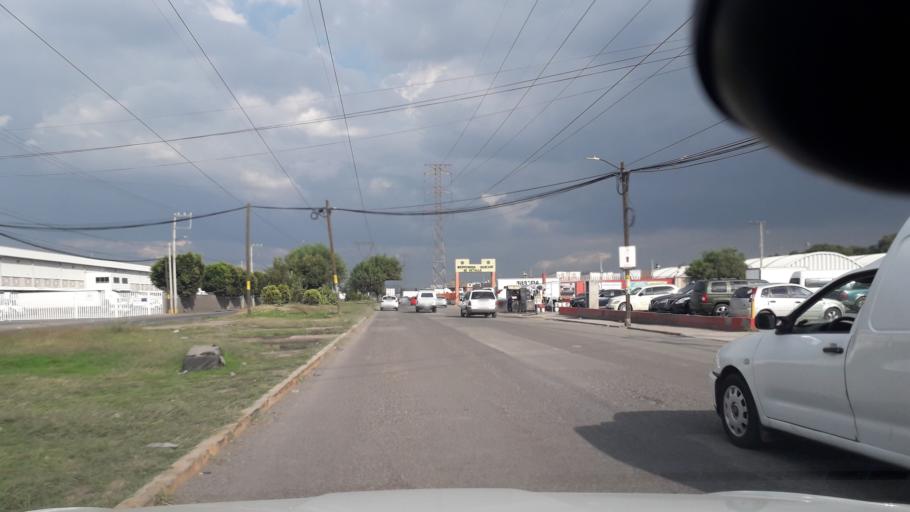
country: MX
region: Mexico
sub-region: Tultitlan
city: Fuentes del Valle
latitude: 19.6398
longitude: -99.1457
